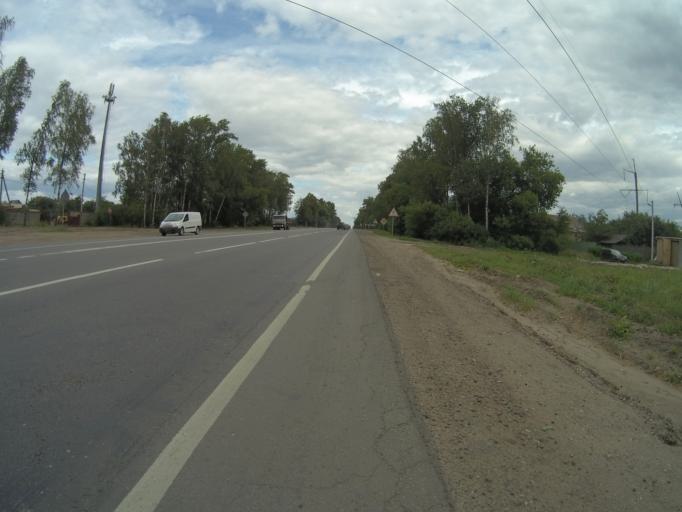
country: RU
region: Vladimir
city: Bogolyubovo
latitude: 56.1858
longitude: 40.5166
